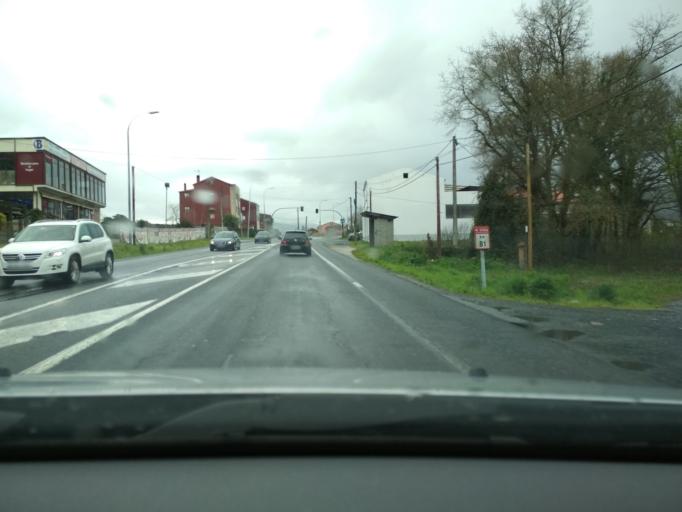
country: ES
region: Galicia
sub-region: Provincia da Coruna
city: Padron
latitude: 42.7529
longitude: -8.6531
